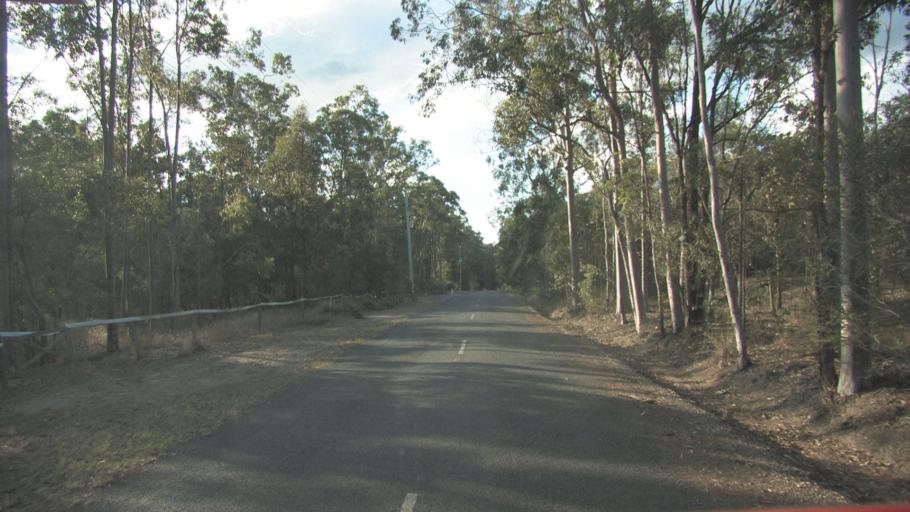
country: AU
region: Queensland
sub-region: Ipswich
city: Springfield Lakes
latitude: -27.6944
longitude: 152.9540
